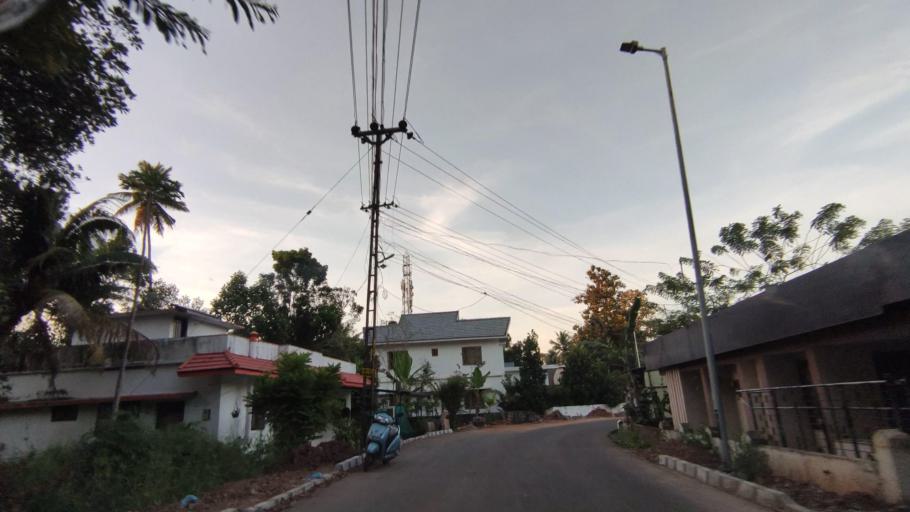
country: IN
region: Kerala
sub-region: Kottayam
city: Kottayam
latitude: 9.6334
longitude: 76.4960
